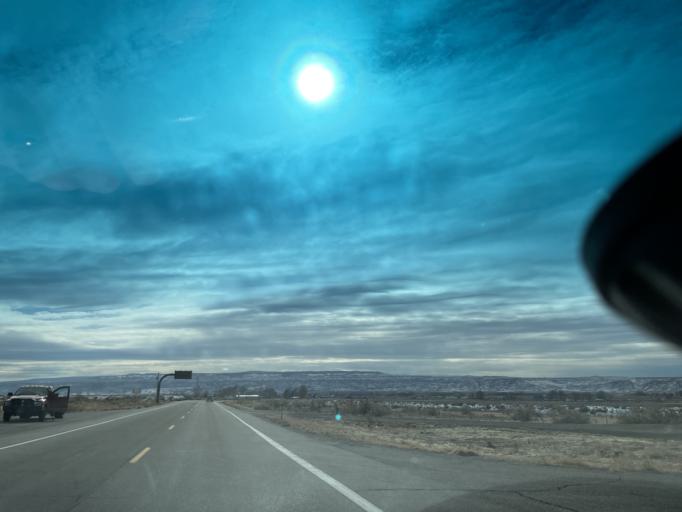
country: US
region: Colorado
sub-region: Mesa County
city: Loma
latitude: 39.2673
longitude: -108.8131
